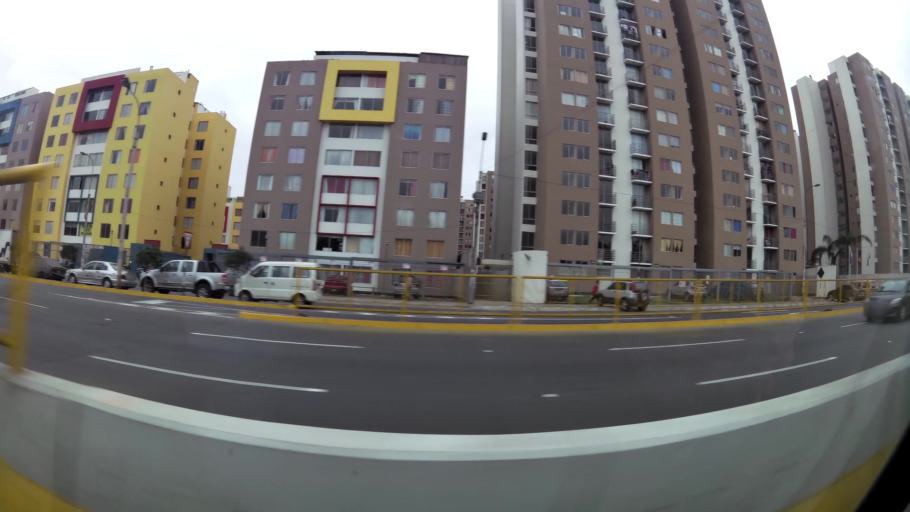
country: PE
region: Callao
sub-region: Callao
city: Callao
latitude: -12.0504
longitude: -77.0804
